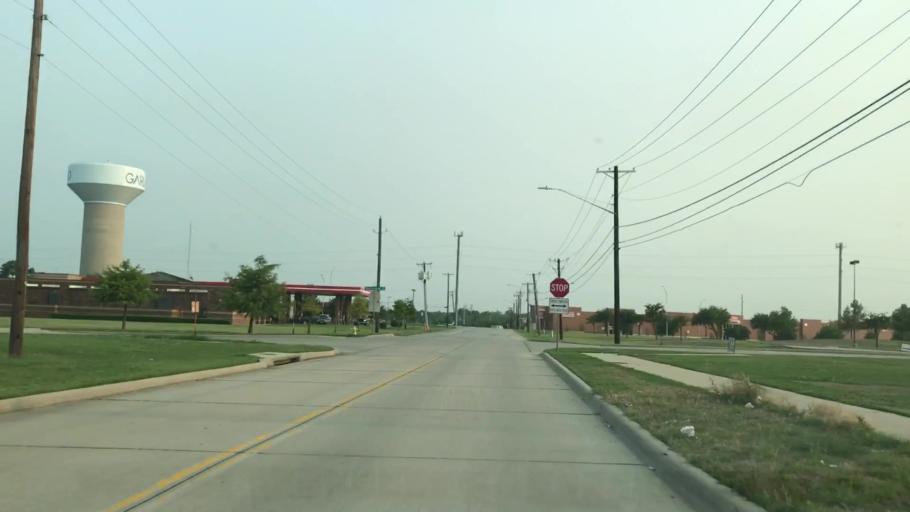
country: US
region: Texas
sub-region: Dallas County
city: Garland
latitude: 32.9126
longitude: -96.6137
